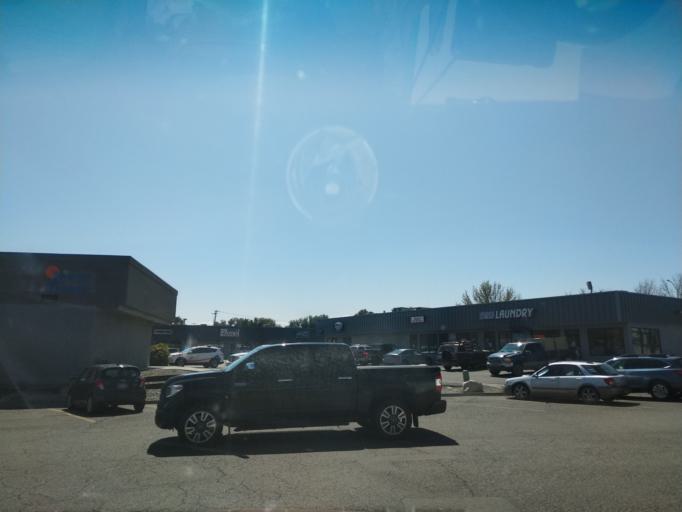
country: US
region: Colorado
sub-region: Delta County
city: Delta
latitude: 38.7472
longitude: -108.0719
